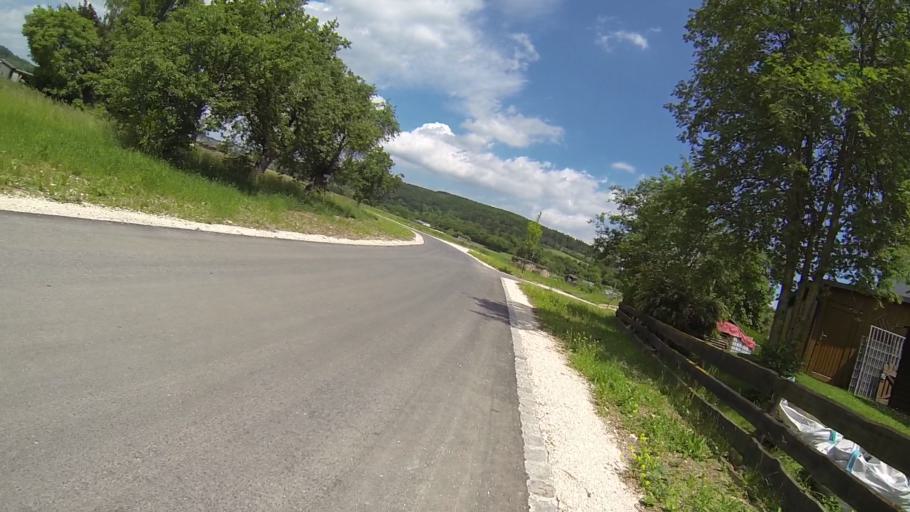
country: DE
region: Baden-Wuerttemberg
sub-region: Regierungsbezirk Stuttgart
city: Bolheim
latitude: 48.6335
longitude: 10.1610
